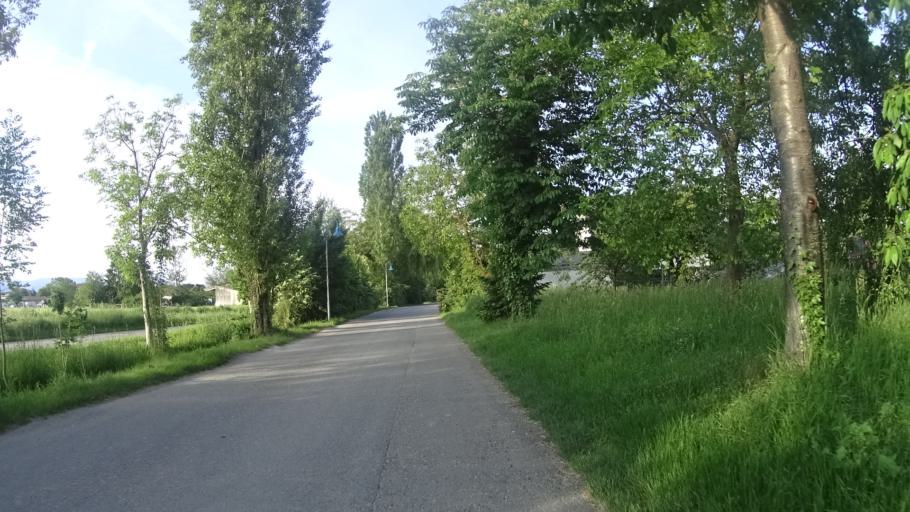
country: DE
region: Baden-Wuerttemberg
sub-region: Freiburg Region
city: Hartheim
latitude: 47.9389
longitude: 7.6469
